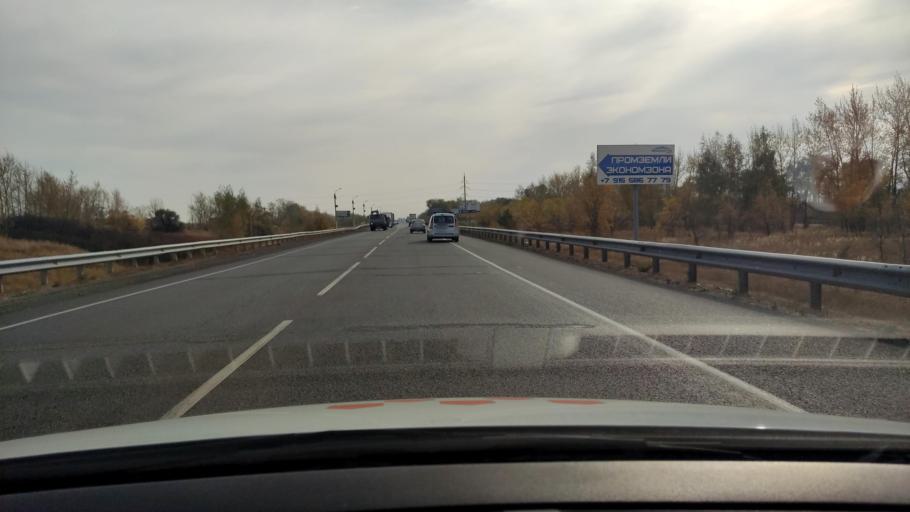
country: RU
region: Voronezj
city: Novaya Usman'
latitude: 51.6957
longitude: 39.4391
